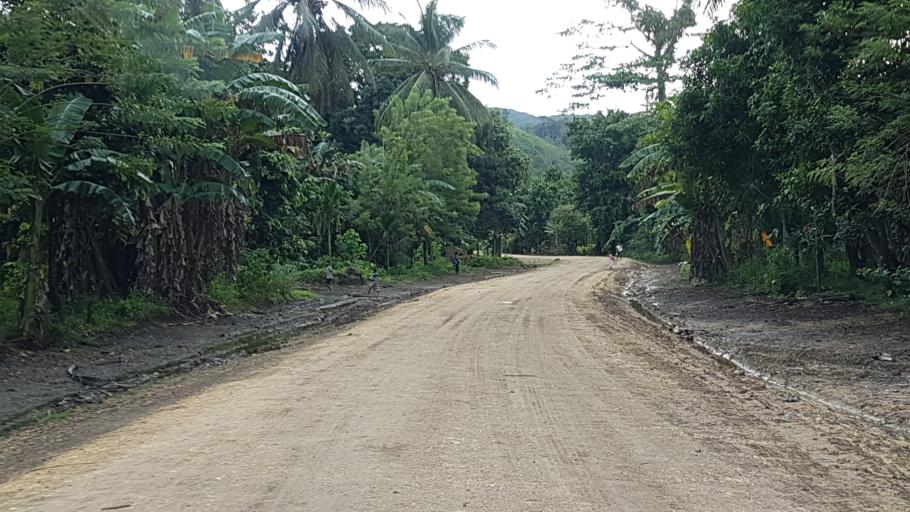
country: PG
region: Milne Bay
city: Alotau
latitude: -10.2989
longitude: 150.7308
